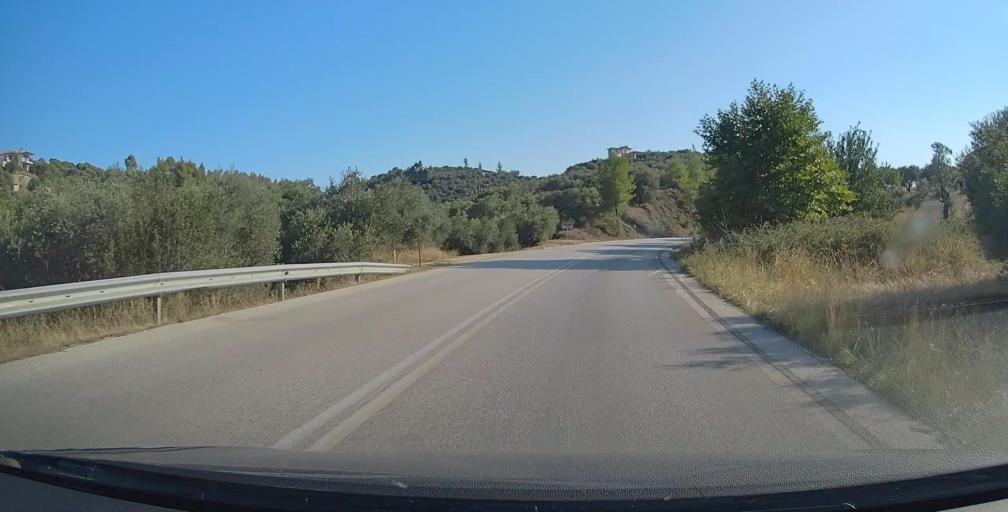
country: GR
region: Central Macedonia
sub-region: Nomos Chalkidikis
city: Neos Marmaras
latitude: 40.0837
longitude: 23.8091
